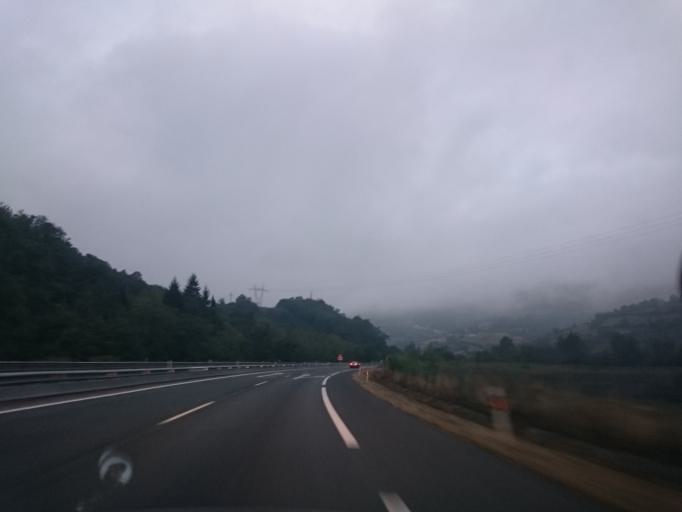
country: ES
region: Asturias
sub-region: Province of Asturias
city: Pola de Lena
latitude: 43.1850
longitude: -5.8011
